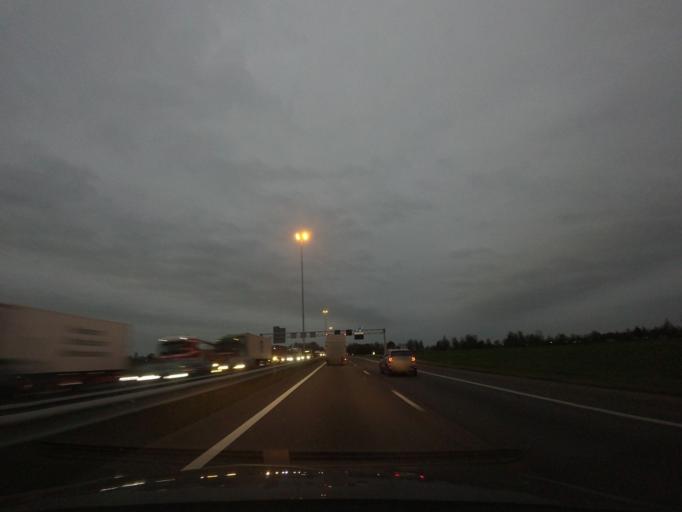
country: NL
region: South Holland
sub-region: Gemeente Gorinchem
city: Gorinchem
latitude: 51.8823
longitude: 4.9705
